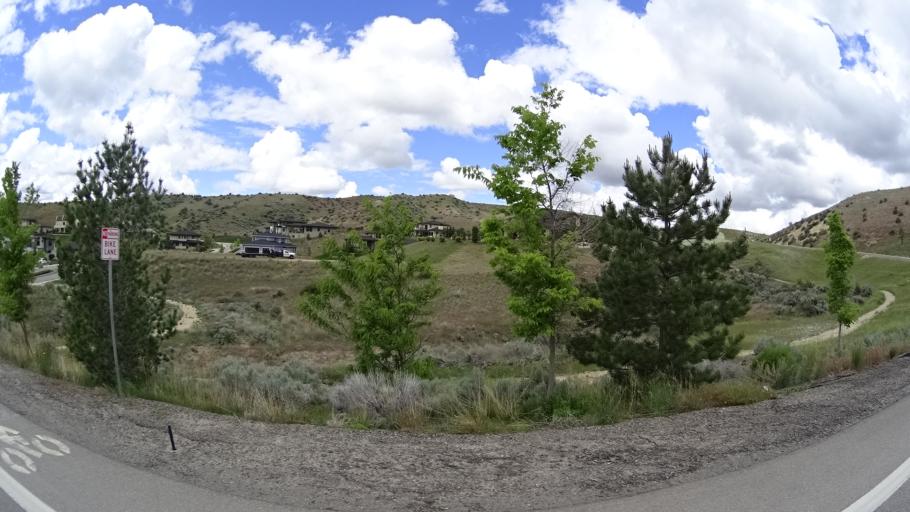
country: US
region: Idaho
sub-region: Ada County
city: Boise
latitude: 43.6609
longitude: -116.1896
